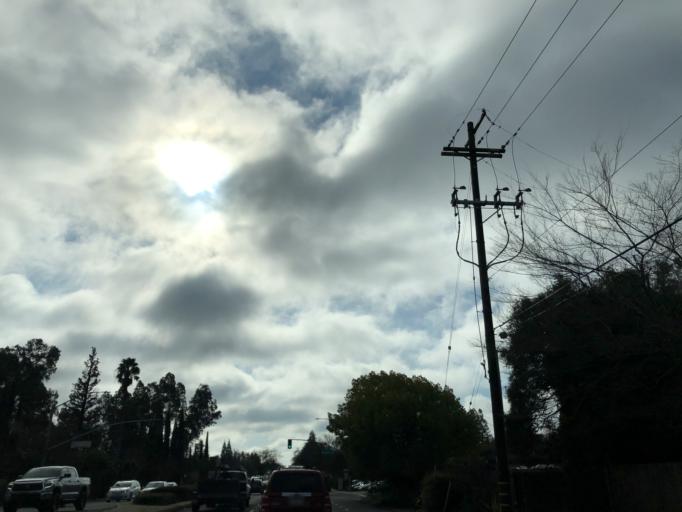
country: US
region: California
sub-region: Sacramento County
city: Arden-Arcade
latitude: 38.5821
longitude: -121.3830
